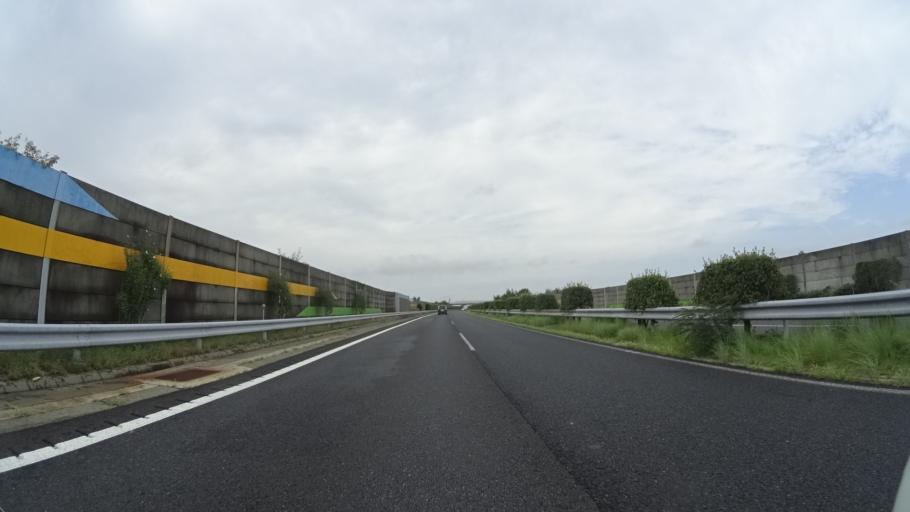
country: JP
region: Hyogo
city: Yashiro
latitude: 34.9318
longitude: 134.9155
